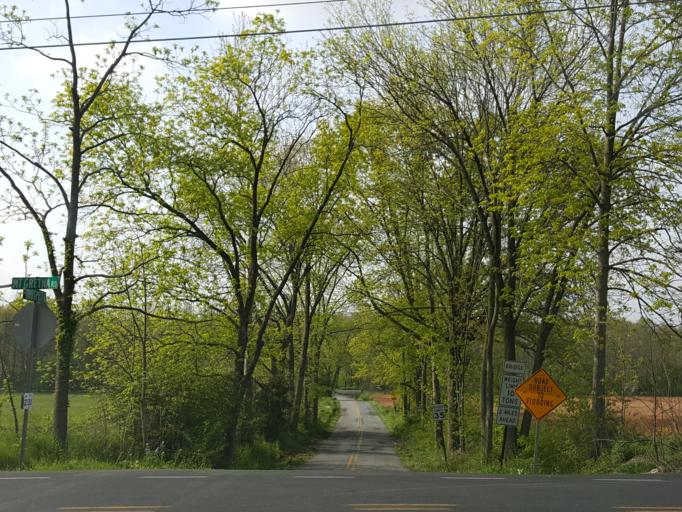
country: US
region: Pennsylvania
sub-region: Lancaster County
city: Elizabethtown
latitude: 40.1931
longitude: -76.5669
